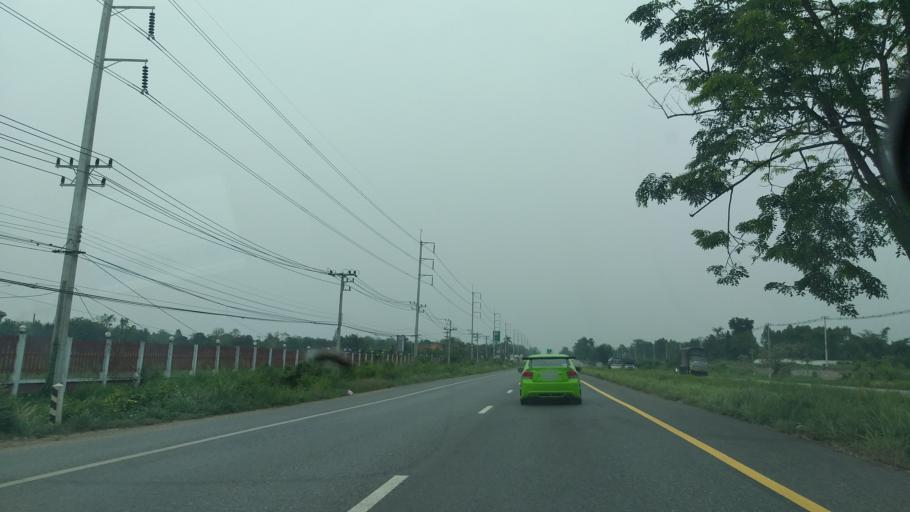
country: TH
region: Chon Buri
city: Ko Chan
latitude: 13.4399
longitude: 101.2832
